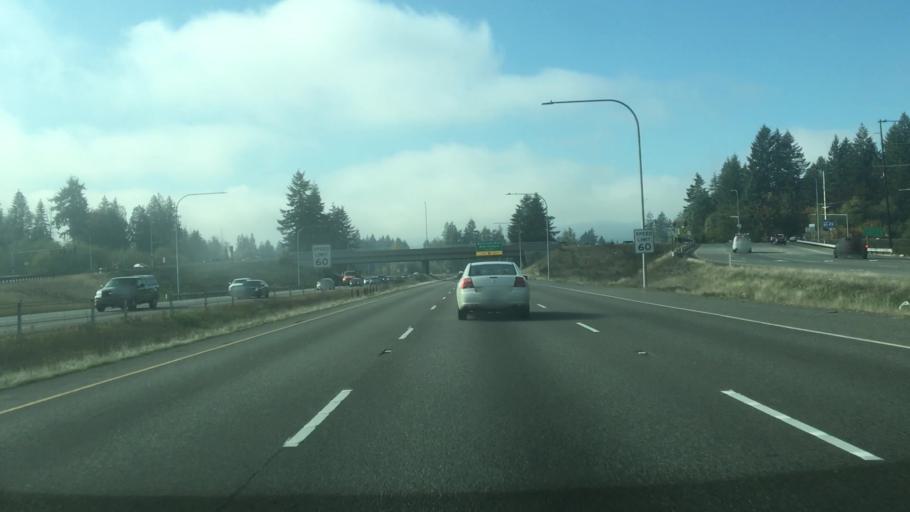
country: US
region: Washington
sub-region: Thurston County
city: Tumwater
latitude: 47.0259
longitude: -122.9204
